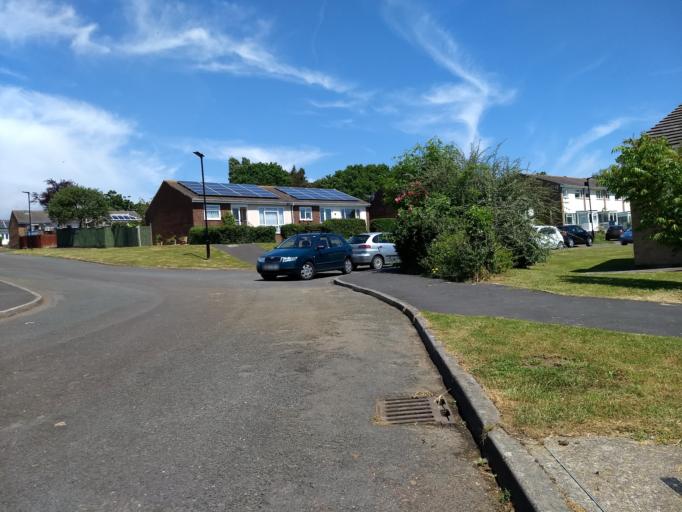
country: GB
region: England
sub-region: Isle of Wight
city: Seaview
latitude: 50.6944
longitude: -1.1115
